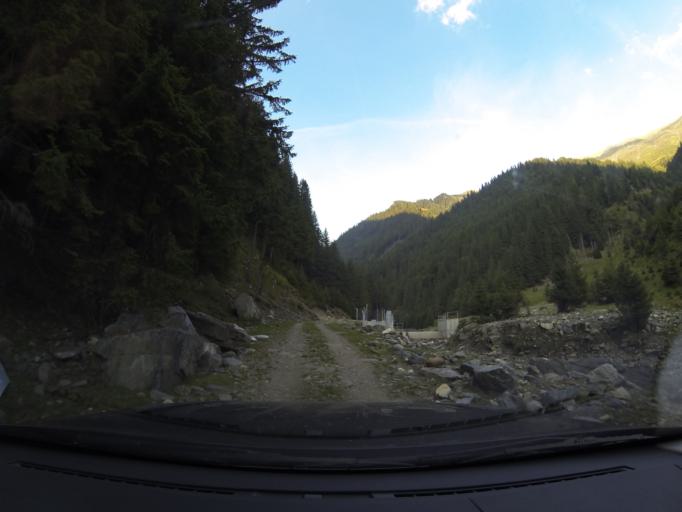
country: RO
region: Brasov
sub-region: Oras Victoria
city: Victoria
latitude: 45.5739
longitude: 24.7019
